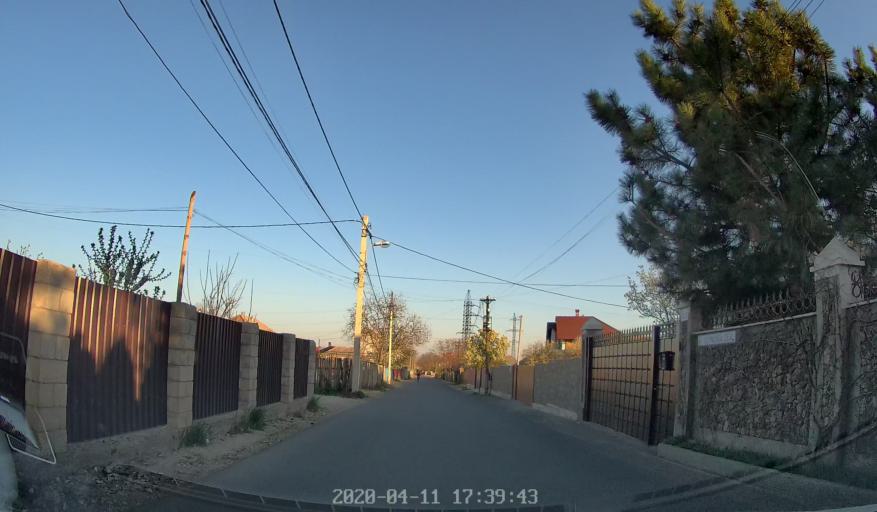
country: MD
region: Laloveni
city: Ialoveni
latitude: 46.9825
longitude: 28.8073
